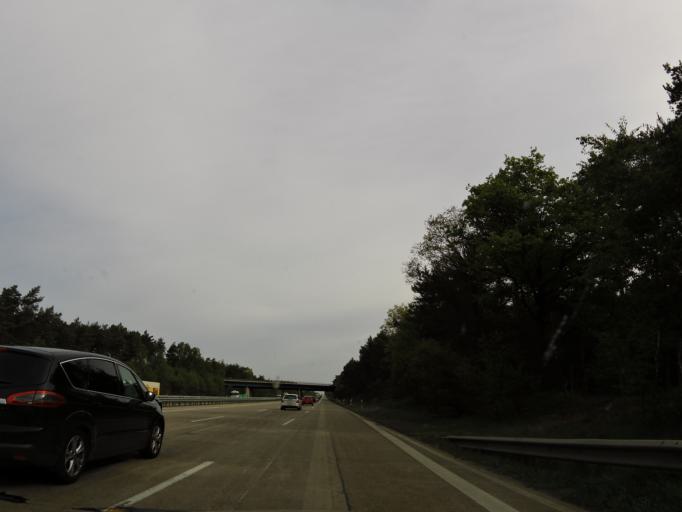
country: DE
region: Lower Saxony
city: Bad Fallingbostel
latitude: 52.7869
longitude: 9.6722
